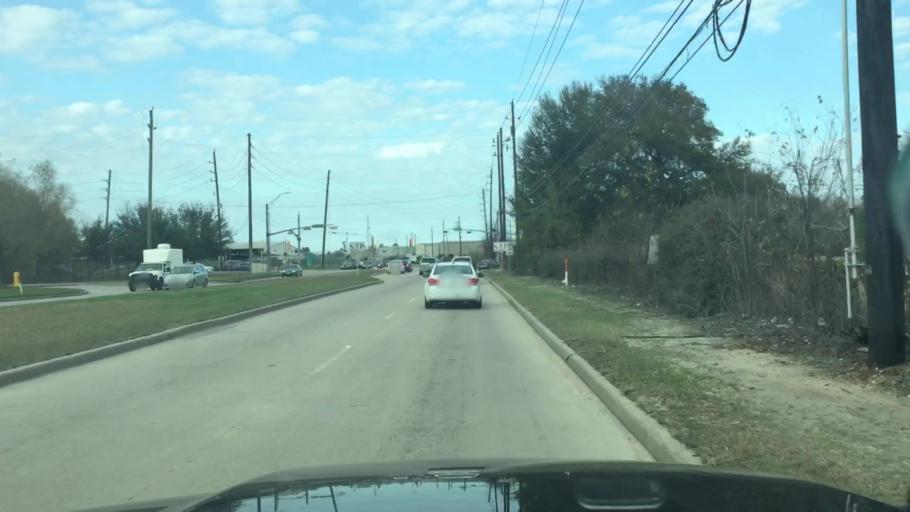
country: US
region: Texas
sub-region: Harris County
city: Hudson
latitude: 29.9241
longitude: -95.5250
